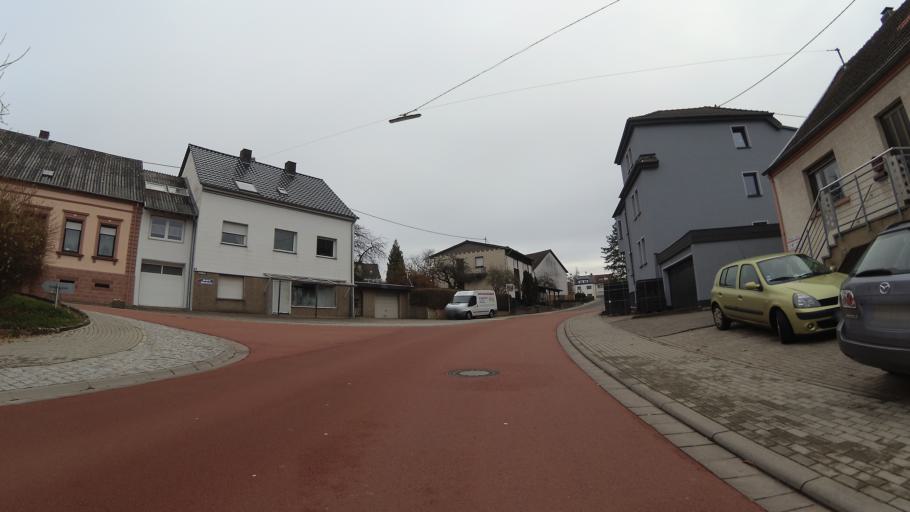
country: DE
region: Saarland
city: Merchweiler
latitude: 49.3563
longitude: 7.0529
